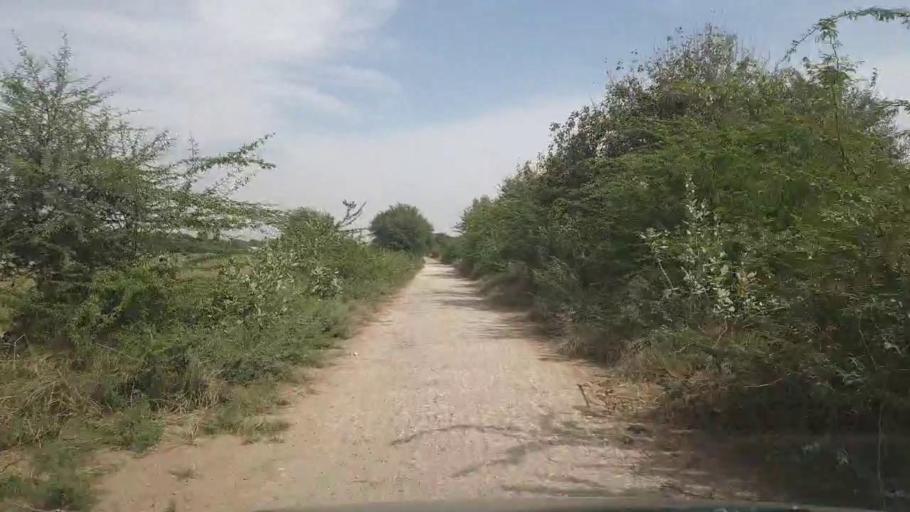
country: PK
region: Sindh
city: Kunri
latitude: 25.2027
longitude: 69.6878
